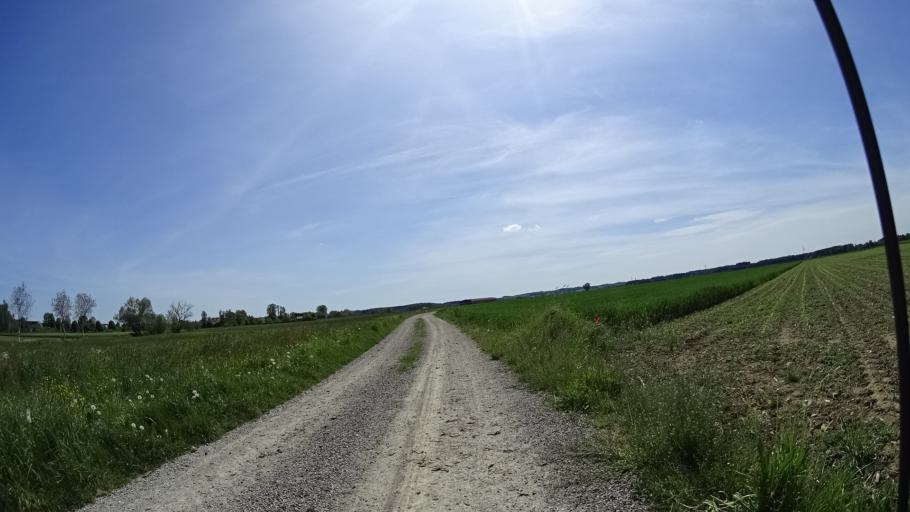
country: DE
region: Bavaria
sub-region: Swabia
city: Pfaffenhofen an der Roth
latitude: 48.3317
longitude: 10.1546
